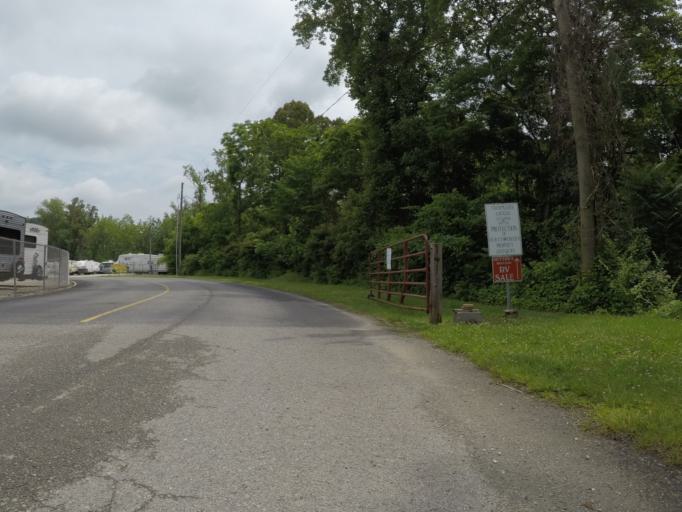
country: US
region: West Virginia
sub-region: Cabell County
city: Pea Ridge
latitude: 38.4165
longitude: -82.3402
